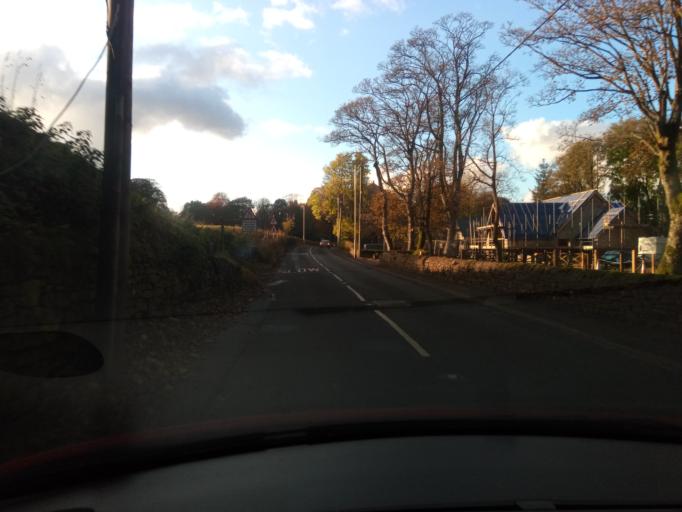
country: GB
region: England
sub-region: County Durham
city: Newbiggin
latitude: 54.7412
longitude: -2.1979
